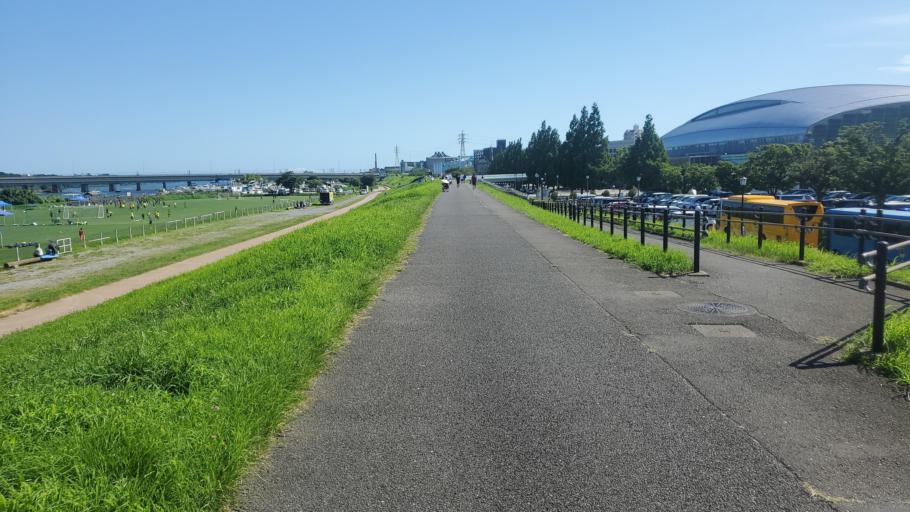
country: JP
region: Kanagawa
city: Hiratsuka
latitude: 35.3376
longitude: 139.3654
